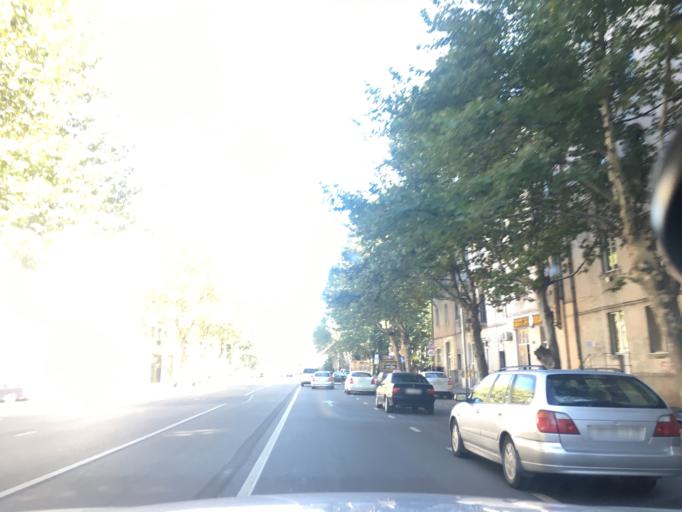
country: GE
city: Zahesi
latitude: 41.7708
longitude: 44.7931
